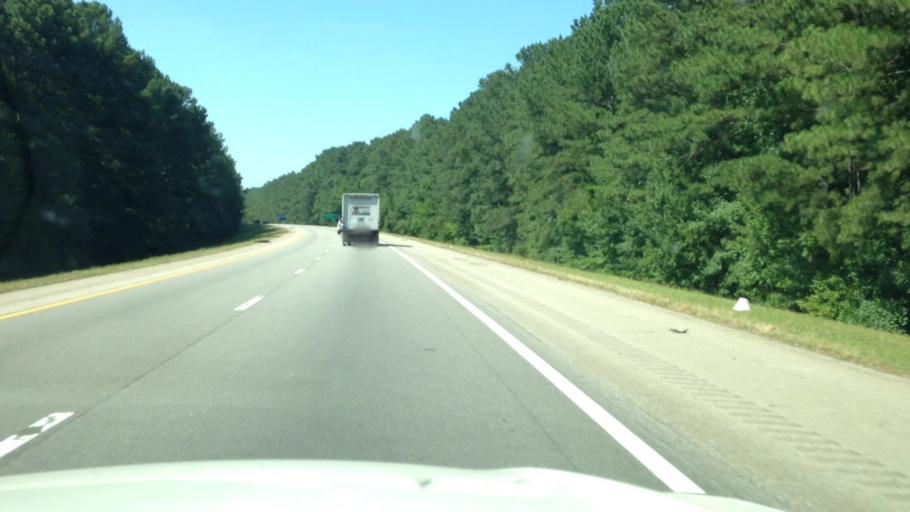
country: US
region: North Carolina
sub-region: Wilson County
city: Wilson
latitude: 35.7518
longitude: -78.0037
